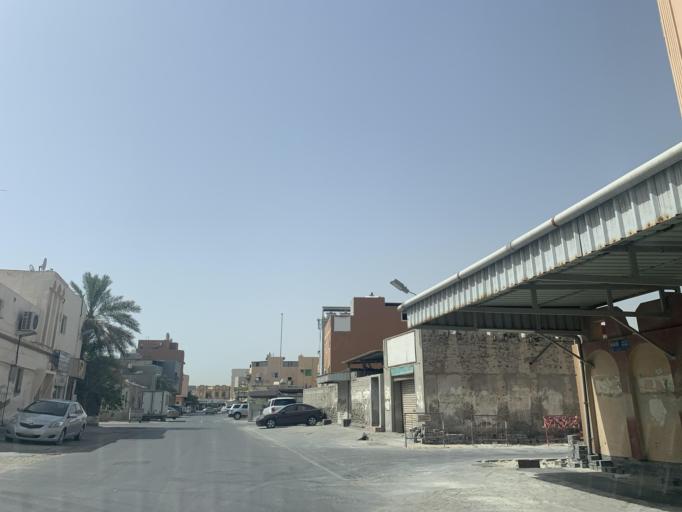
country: BH
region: Northern
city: Sitrah
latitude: 26.1609
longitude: 50.6094
